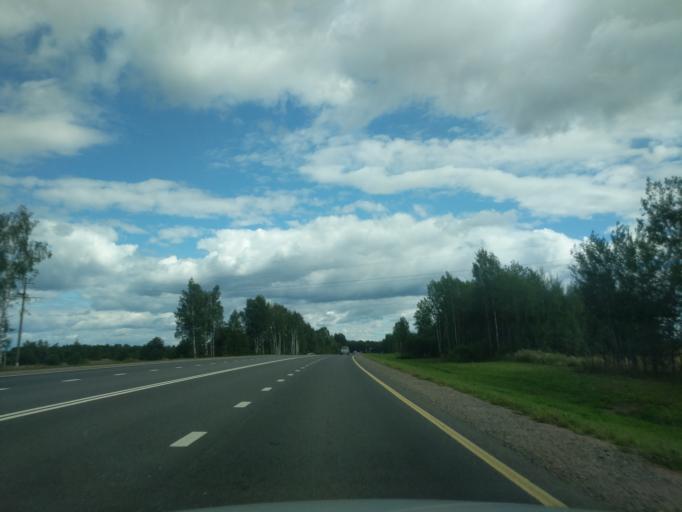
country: RU
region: Kostroma
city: Oktyabr'skiy
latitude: 57.7857
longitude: 41.1016
